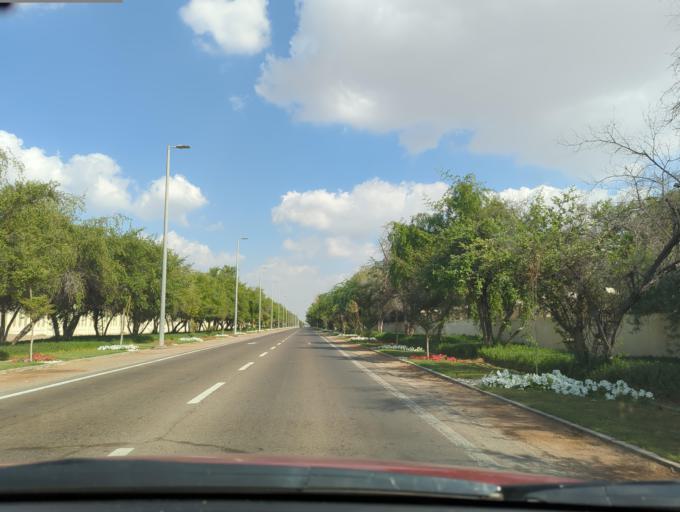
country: AE
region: Abu Dhabi
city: Al Ain
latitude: 24.1685
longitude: 55.6535
